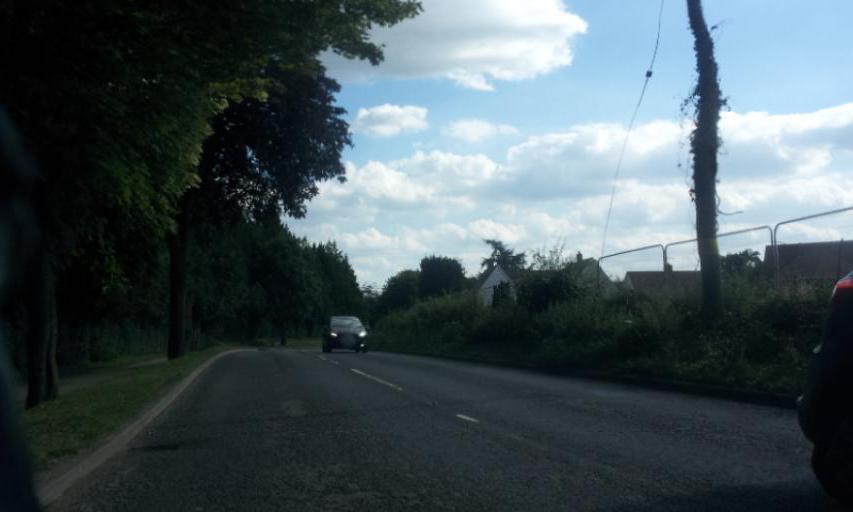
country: GB
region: England
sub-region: Kent
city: Headcorn
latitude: 51.2174
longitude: 0.5928
